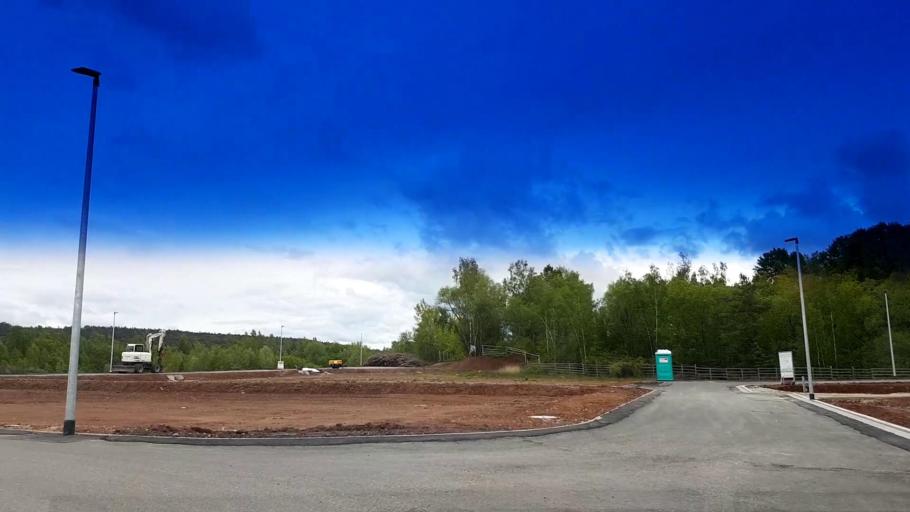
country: DE
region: Bavaria
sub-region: Upper Franconia
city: Bischberg
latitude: 49.9043
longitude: 10.8482
